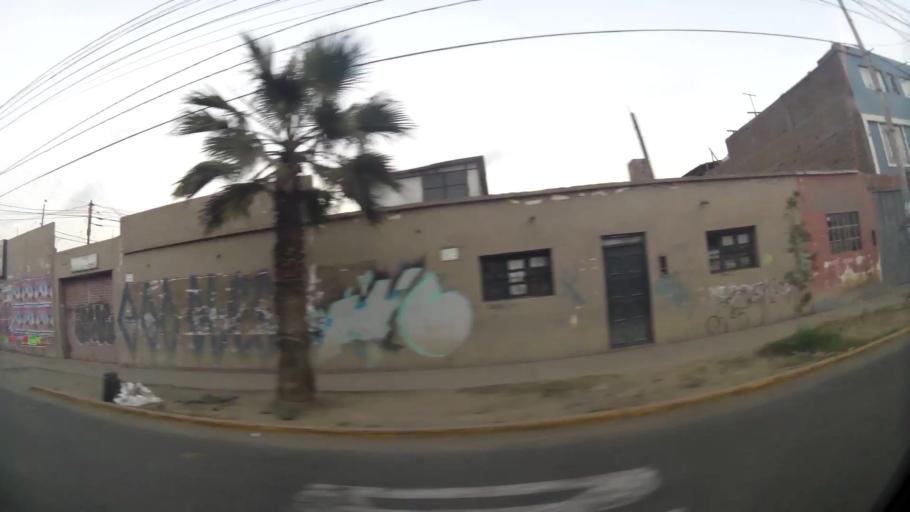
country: PE
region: La Libertad
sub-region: Provincia de Trujillo
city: Trujillo
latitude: -8.1045
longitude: -79.0233
